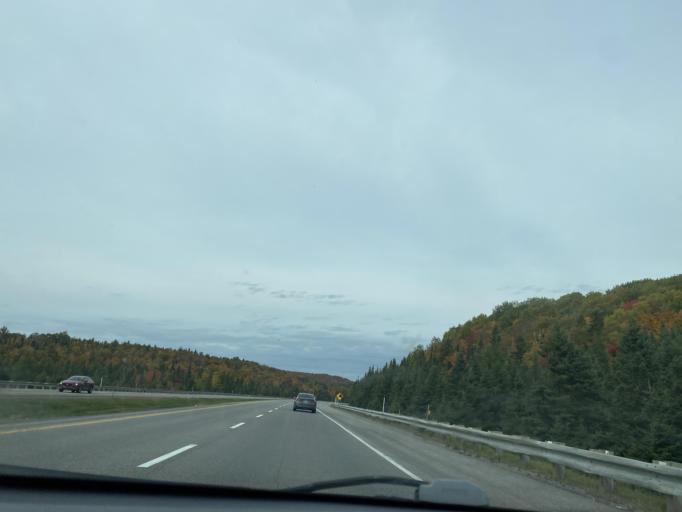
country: CA
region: Quebec
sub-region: Laurentides
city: Val-David
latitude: 45.9990
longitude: -74.2247
